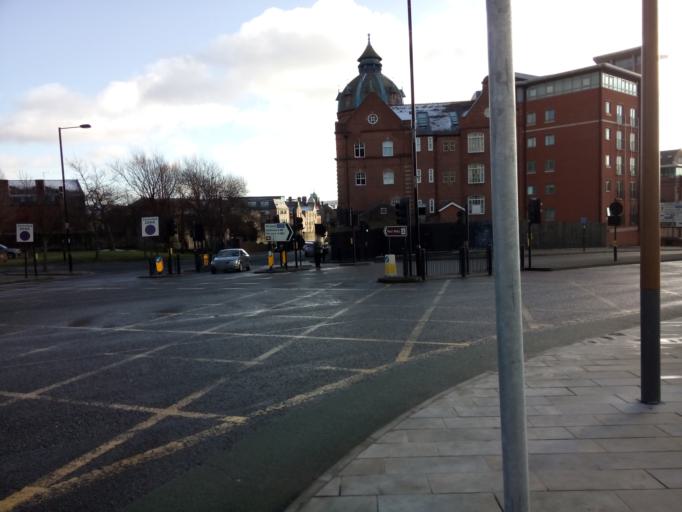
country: GB
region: England
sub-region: Newcastle upon Tyne
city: Newcastle upon Tyne
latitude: 54.9723
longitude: -1.6227
